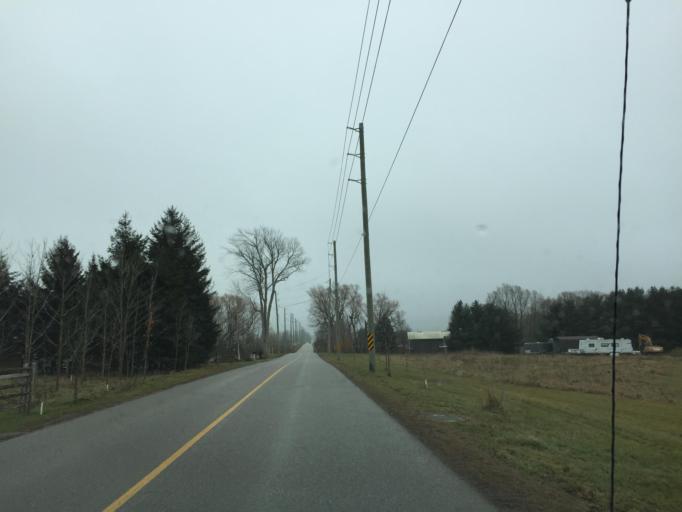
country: CA
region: Ontario
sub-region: Wellington County
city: Guelph
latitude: 43.4917
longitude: -80.3428
